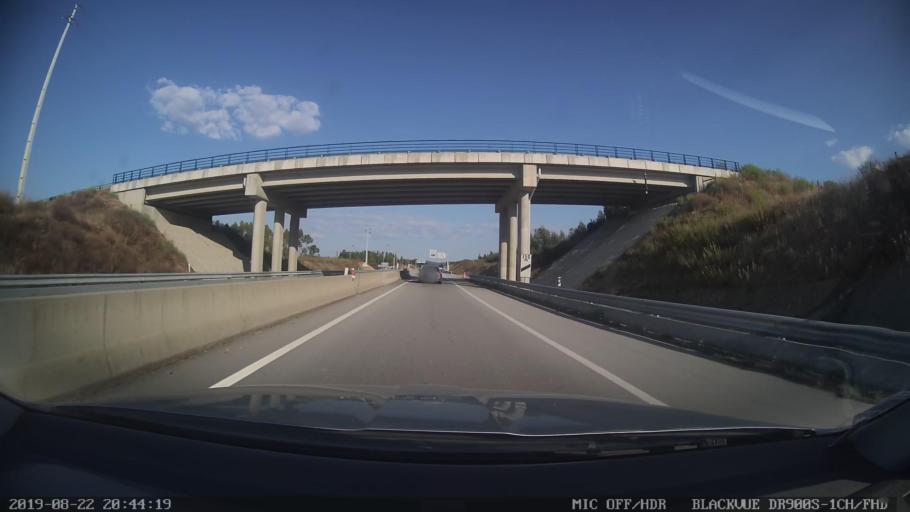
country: PT
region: Castelo Branco
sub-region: Proenca-A-Nova
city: Proenca-a-Nova
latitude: 39.7063
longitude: -7.8490
